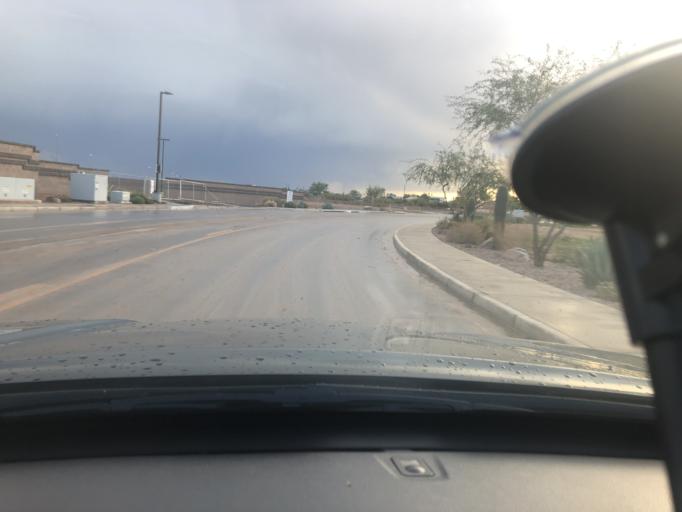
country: US
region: Arizona
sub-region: Maricopa County
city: Scottsdale
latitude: 33.4867
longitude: -111.8898
